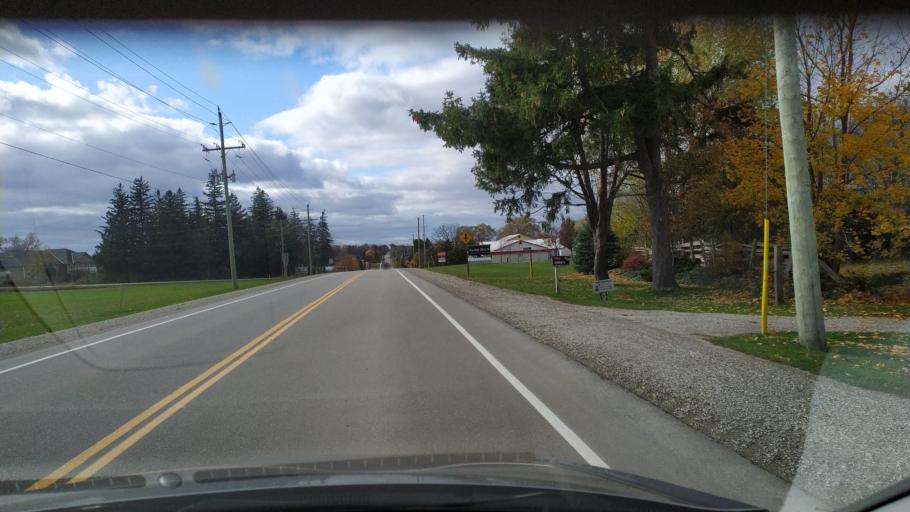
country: CA
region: Ontario
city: Stratford
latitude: 43.2631
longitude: -81.1102
